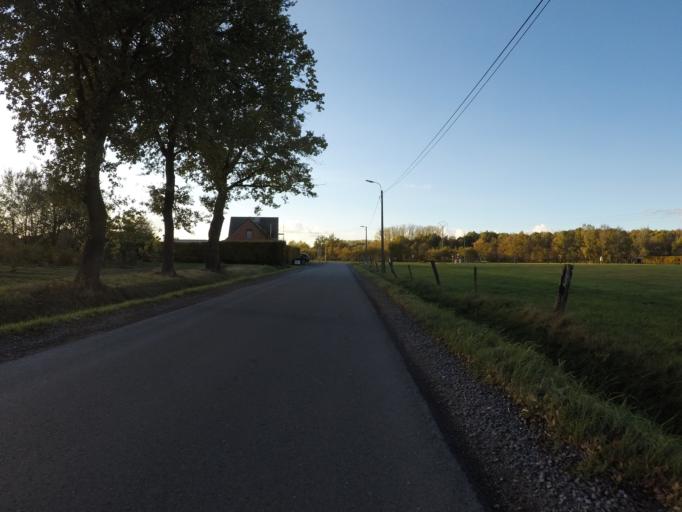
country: BE
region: Flanders
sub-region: Provincie Vlaams-Brabant
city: Begijnendijk
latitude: 51.0077
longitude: 4.8036
